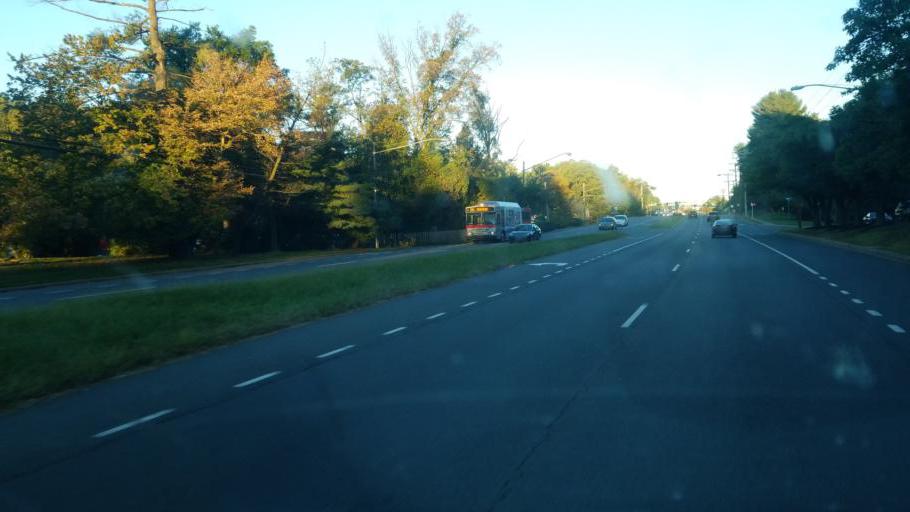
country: US
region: Virginia
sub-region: Fairfax County
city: Annandale
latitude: 38.8262
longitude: -77.1762
